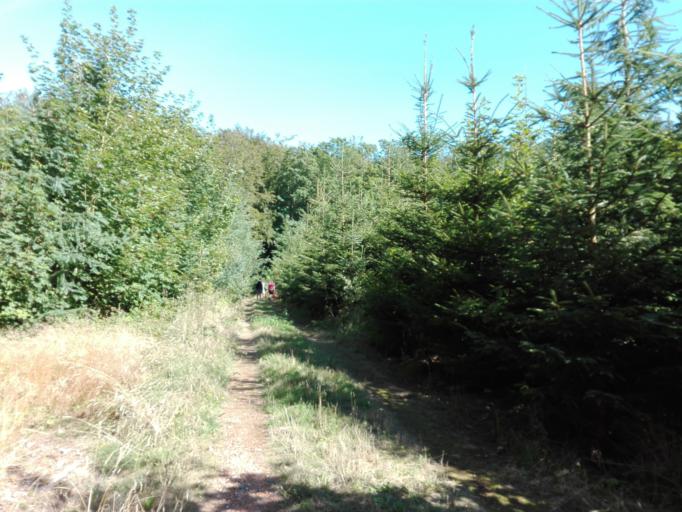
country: DK
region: Central Jutland
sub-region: Odder Kommune
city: Odder
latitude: 55.9526
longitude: 10.0844
